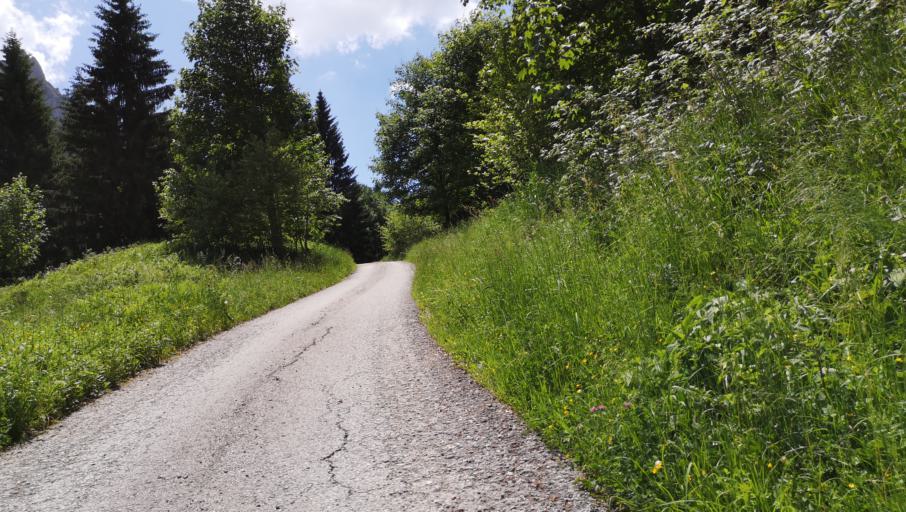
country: IT
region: Friuli Venezia Giulia
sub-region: Provincia di Udine
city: Pontebba
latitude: 46.5055
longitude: 13.2469
